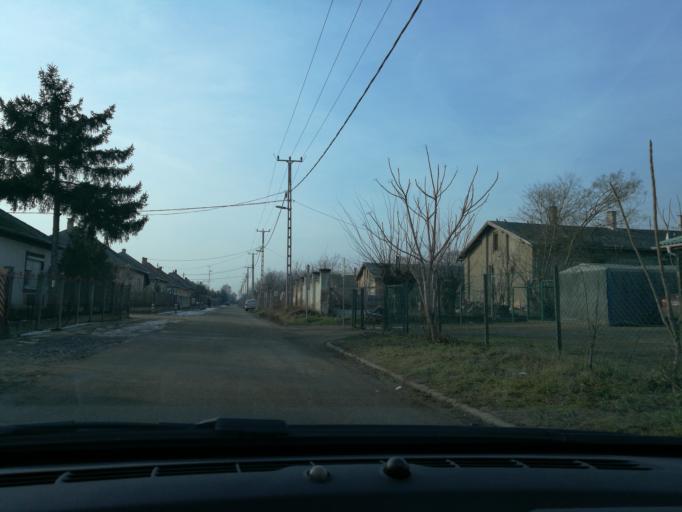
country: HU
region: Szabolcs-Szatmar-Bereg
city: Nyiregyhaza
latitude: 47.9383
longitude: 21.7059
